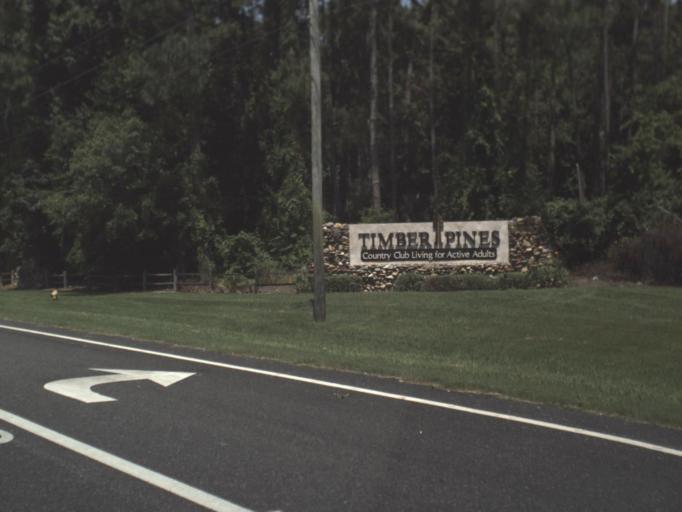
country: US
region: Florida
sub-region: Hernando County
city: Timber Pines
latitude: 28.4705
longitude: -82.6182
